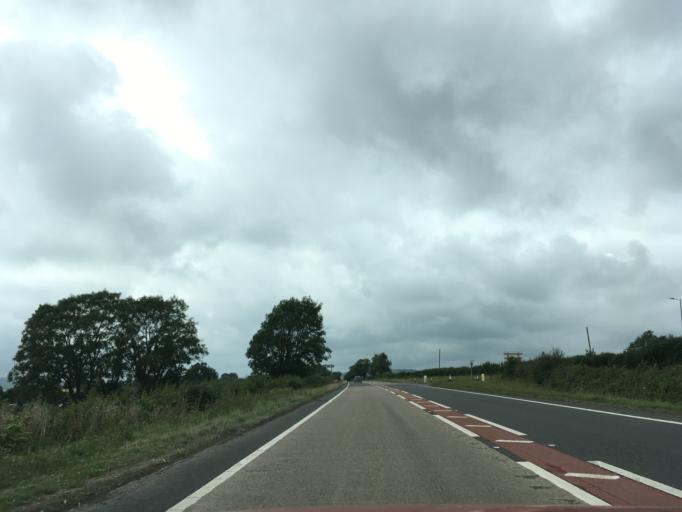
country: GB
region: Wales
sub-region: Carmarthenshire
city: Llanddowror
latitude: 51.8216
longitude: -4.5227
